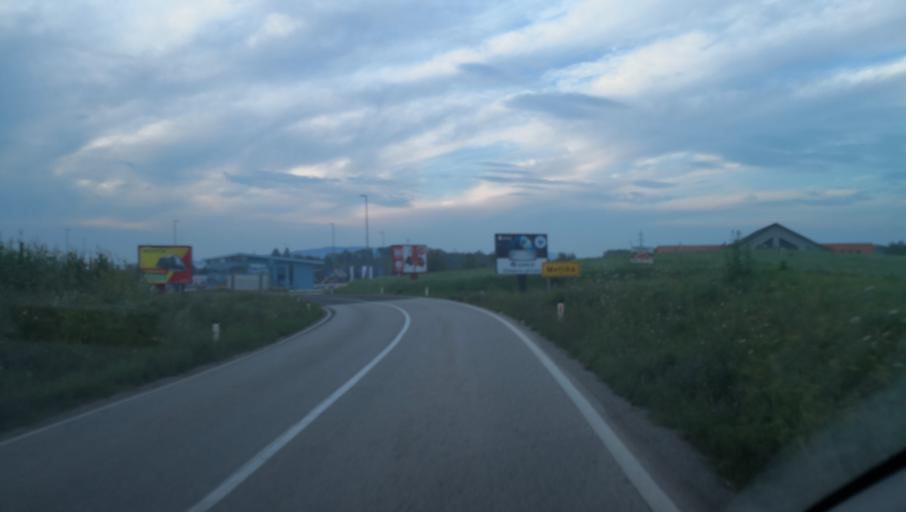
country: SI
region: Metlika
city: Metlika
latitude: 45.6512
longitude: 15.3024
